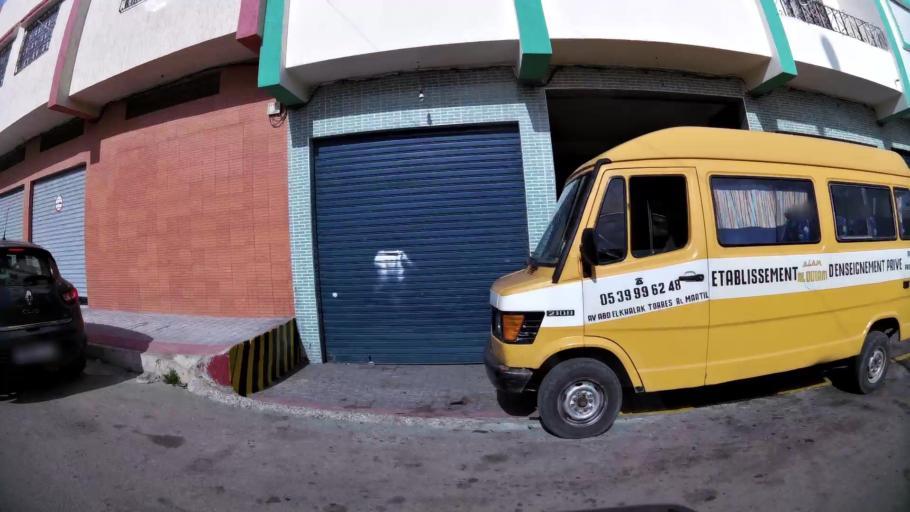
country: MA
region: Tanger-Tetouan
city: Tetouan
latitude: 35.5930
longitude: -5.3479
